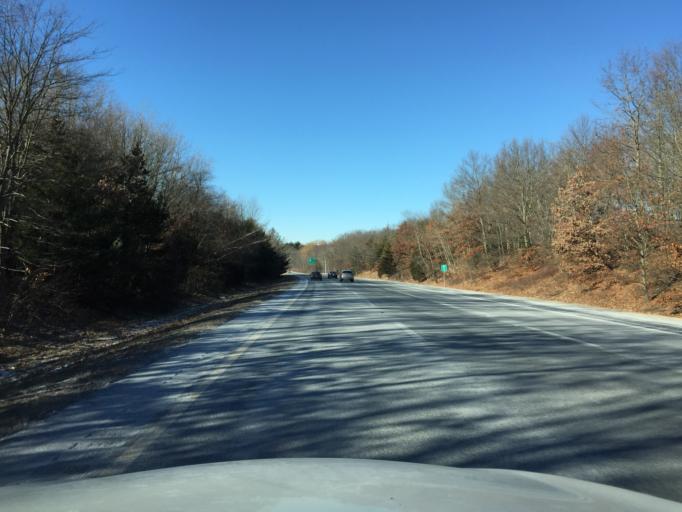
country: US
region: Massachusetts
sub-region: Norfolk County
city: Wrentham
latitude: 42.0354
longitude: -71.2909
